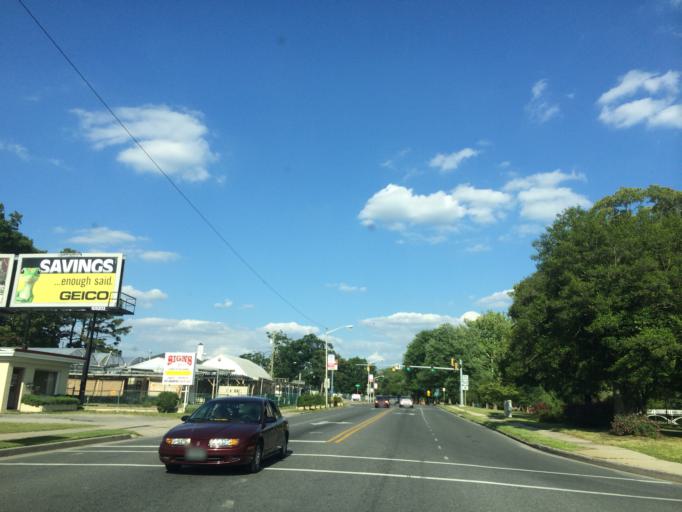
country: US
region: Maryland
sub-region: Wicomico County
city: Salisbury
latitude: 38.3655
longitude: -75.5927
